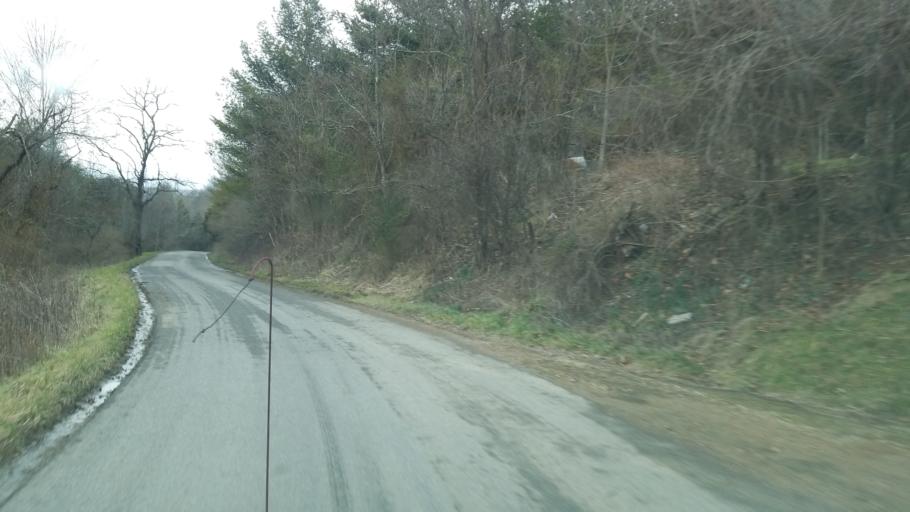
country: US
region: Virginia
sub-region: Giles County
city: Pearisburg
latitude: 37.2256
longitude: -80.6979
